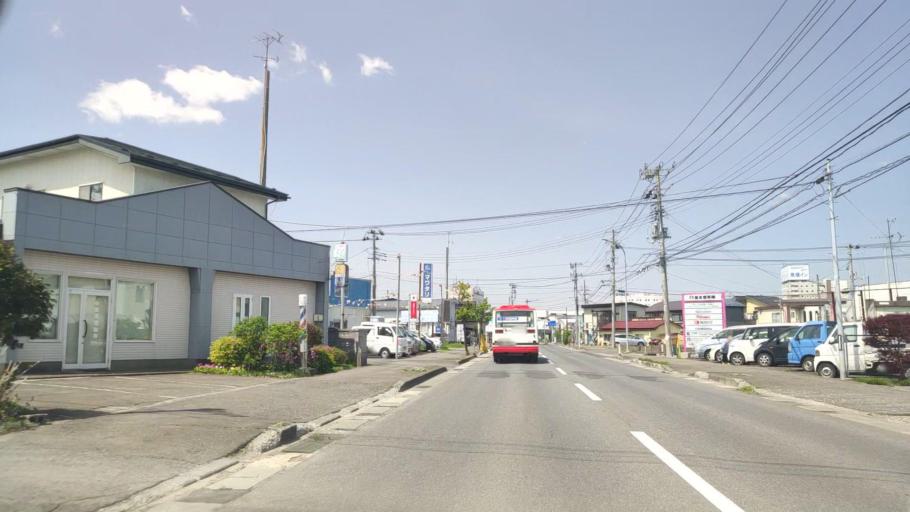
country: JP
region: Aomori
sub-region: Hachinohe Shi
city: Uchimaru
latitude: 40.5065
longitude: 141.4370
